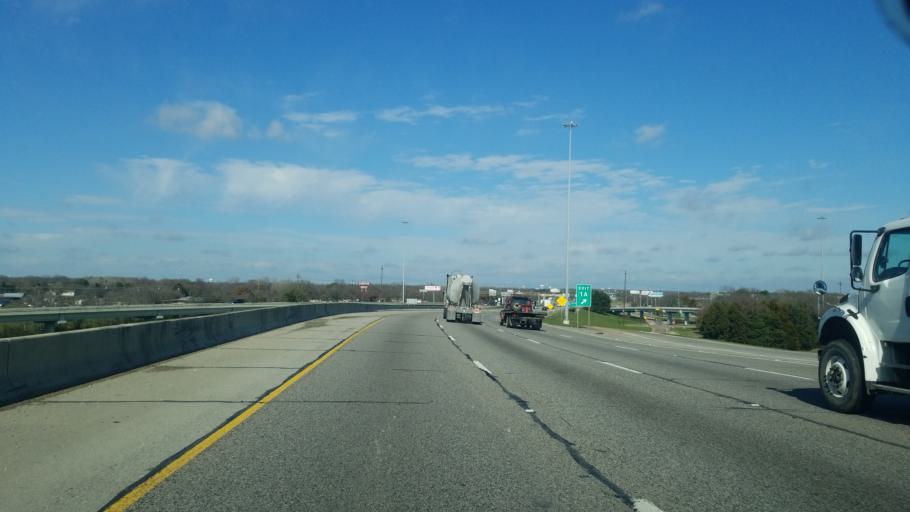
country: US
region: Texas
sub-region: Dallas County
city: Balch Springs
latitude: 32.7019
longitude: -96.6253
